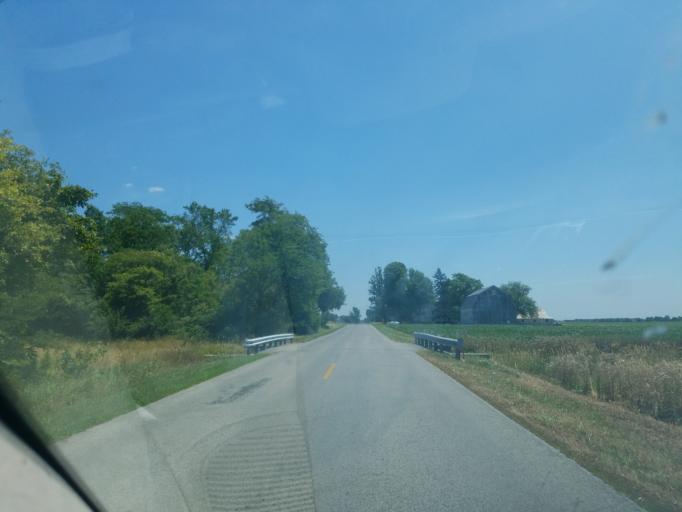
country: US
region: Ohio
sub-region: Allen County
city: Elida
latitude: 40.7871
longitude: -84.2761
